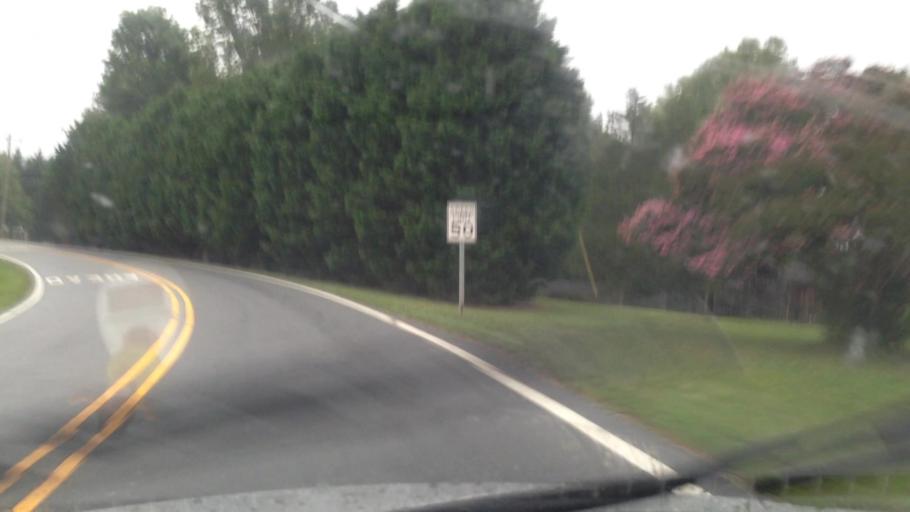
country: US
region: North Carolina
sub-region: Forsyth County
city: Walkertown
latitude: 36.1522
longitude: -80.1273
